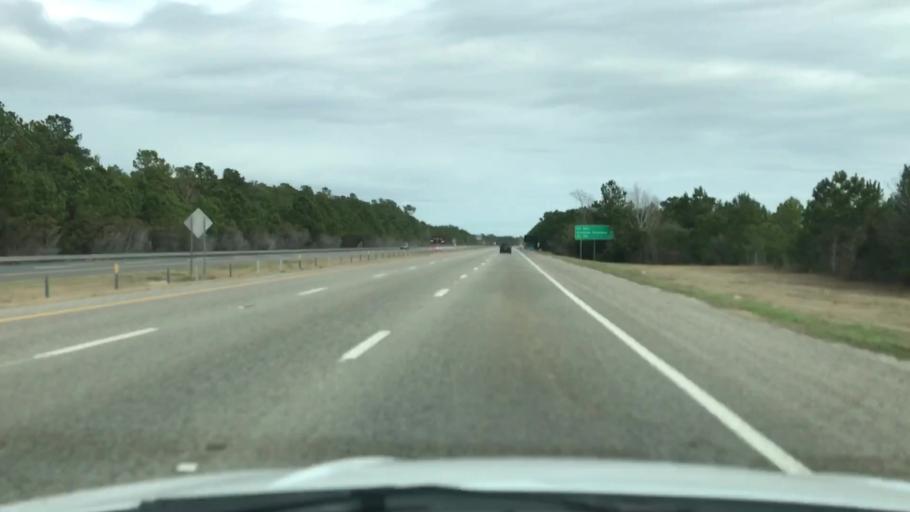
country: US
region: South Carolina
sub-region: Horry County
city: Socastee
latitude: 33.7156
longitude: -79.0024
